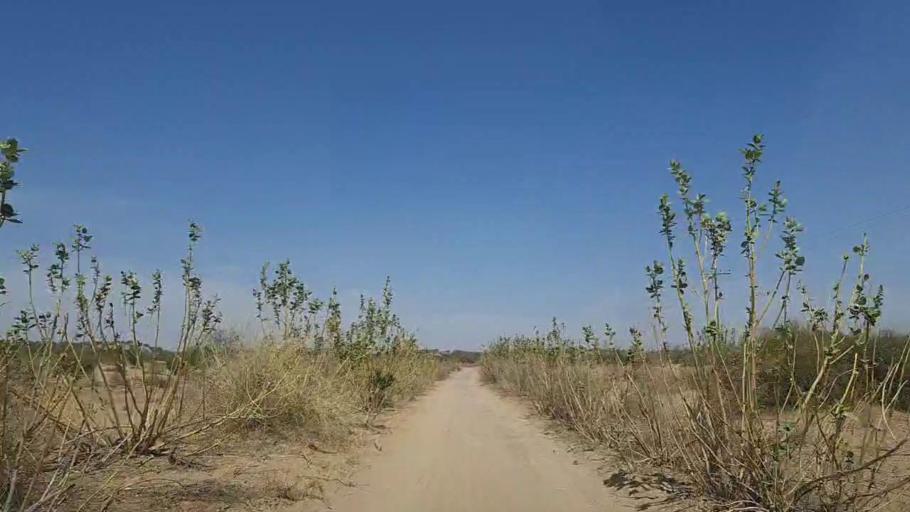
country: PK
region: Sindh
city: Mithi
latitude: 24.8454
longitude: 69.6685
